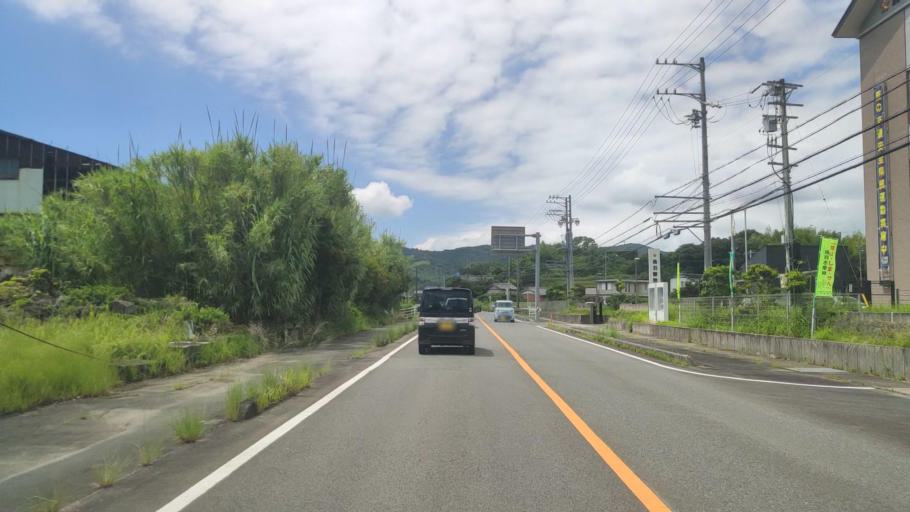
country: JP
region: Mie
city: Toba
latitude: 34.4385
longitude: 136.8415
